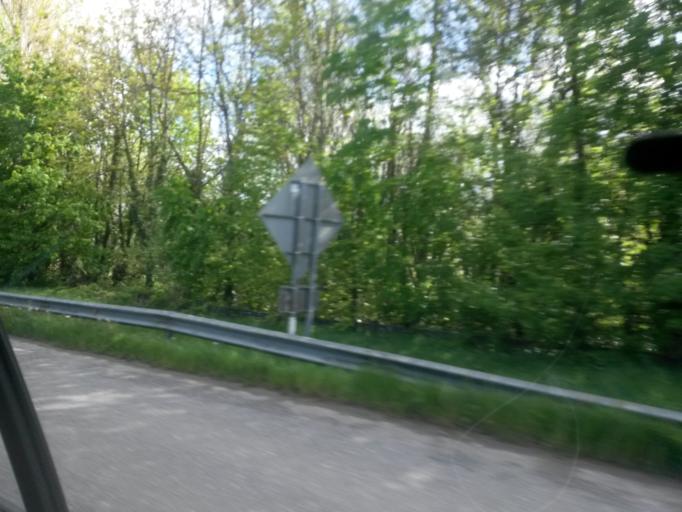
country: IE
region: Leinster
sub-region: Loch Garman
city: Enniscorthy
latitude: 52.5167
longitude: -6.5650
